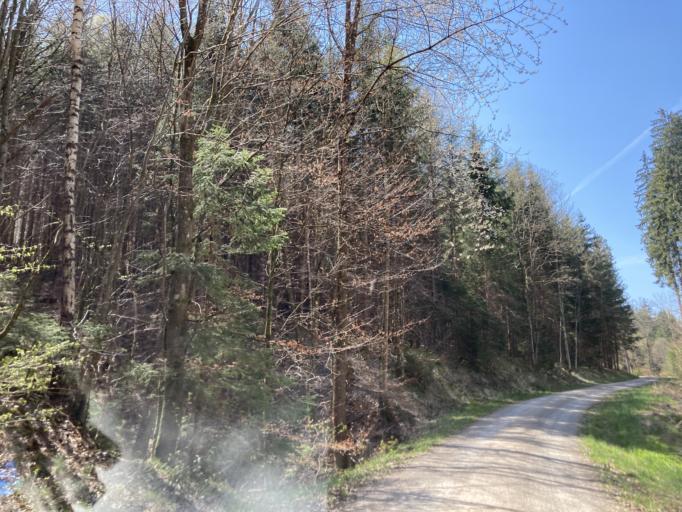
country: DE
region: Baden-Wuerttemberg
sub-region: Tuebingen Region
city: Tuebingen
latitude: 48.5547
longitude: 9.0472
